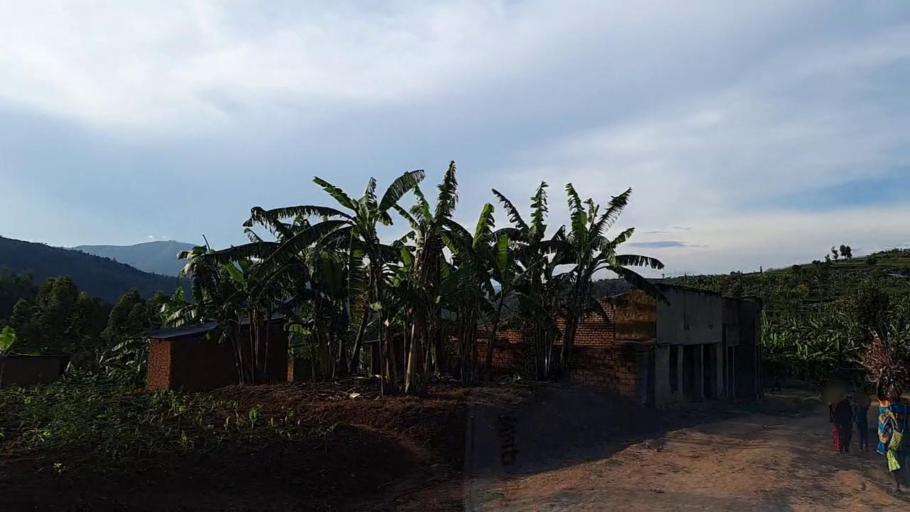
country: RW
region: Southern Province
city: Gikongoro
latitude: -2.3977
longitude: 29.5541
